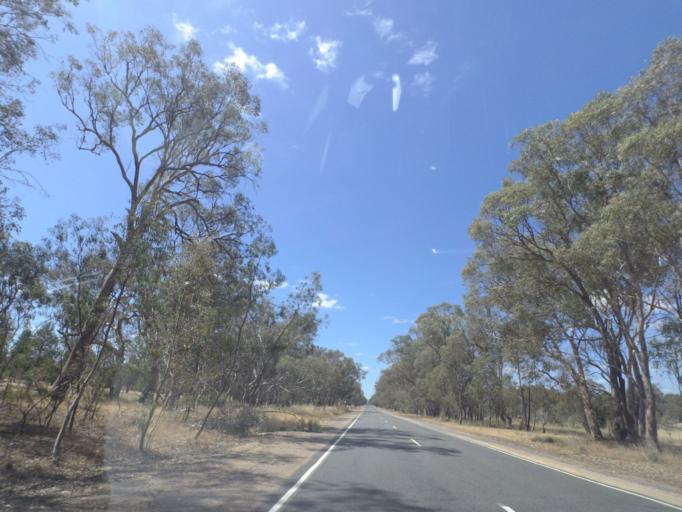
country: AU
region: Victoria
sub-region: Wangaratta
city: Wangaratta
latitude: -36.4324
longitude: 146.2523
